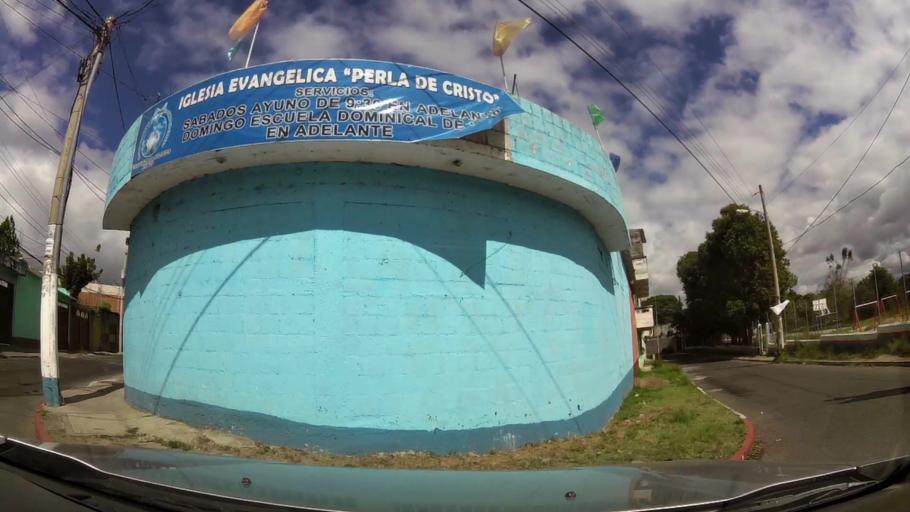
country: GT
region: Guatemala
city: Guatemala City
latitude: 14.6812
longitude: -90.5421
